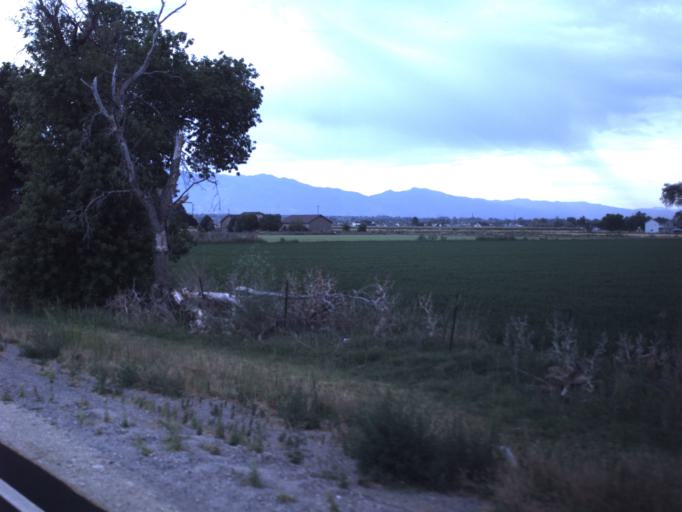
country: US
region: Utah
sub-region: Weber County
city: Hooper
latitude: 41.1639
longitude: -112.1068
